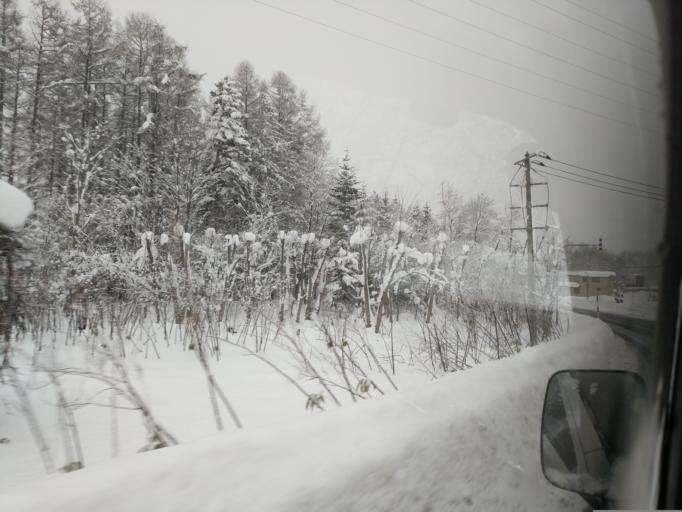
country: JP
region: Hokkaido
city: Niseko Town
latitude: 42.8892
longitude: 140.7398
